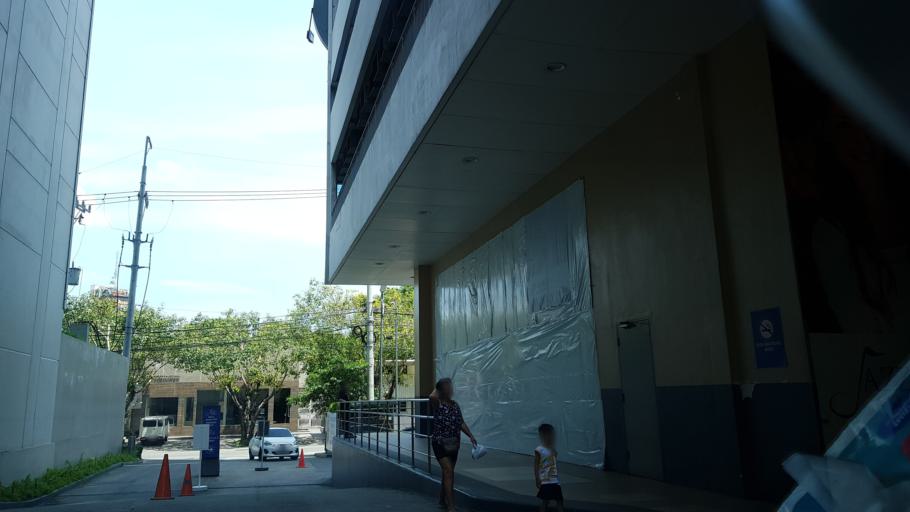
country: PH
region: Metro Manila
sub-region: Makati City
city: Makati City
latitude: 14.5645
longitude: 121.0221
